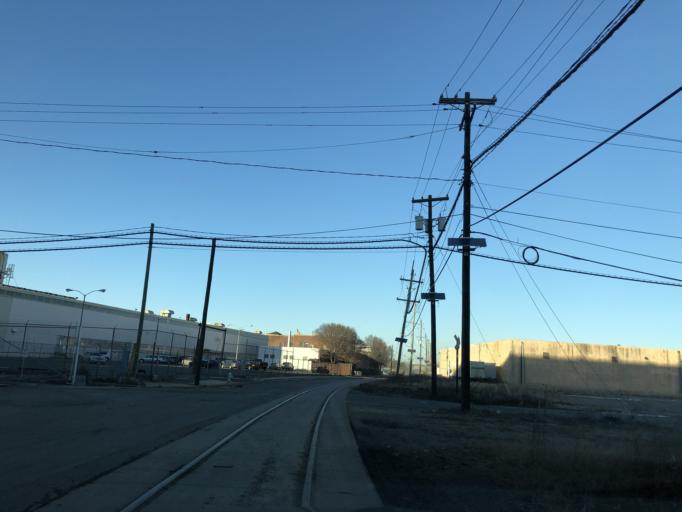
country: US
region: New Jersey
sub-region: Camden County
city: Camden
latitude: 39.9299
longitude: -75.1293
